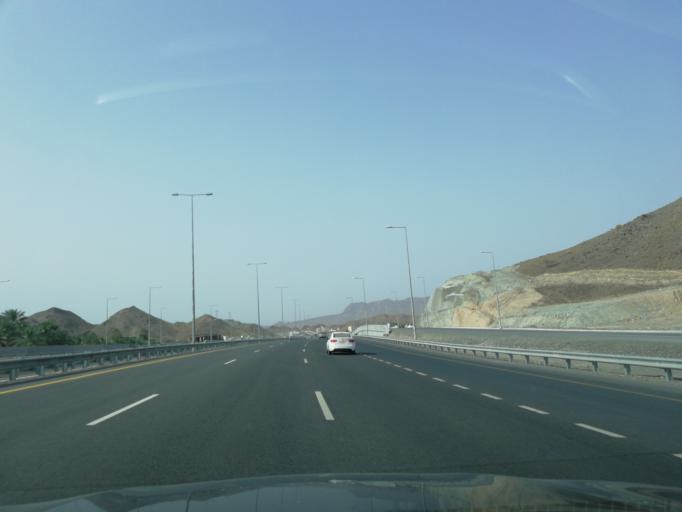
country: OM
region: Muhafazat ad Dakhiliyah
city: Bidbid
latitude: 23.4061
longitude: 58.0990
